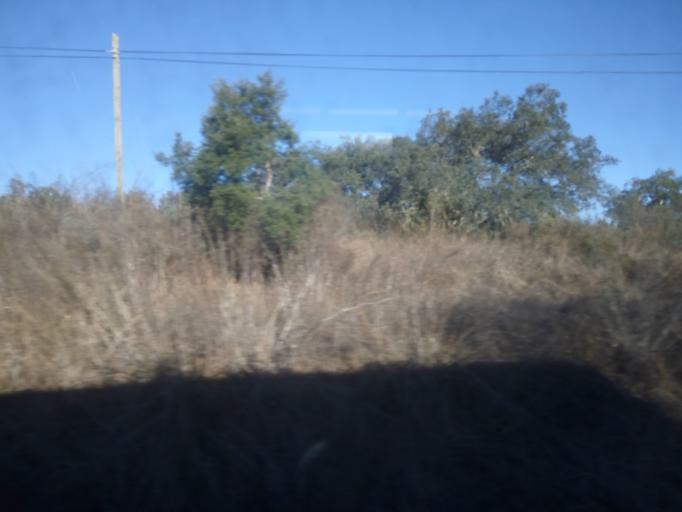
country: PT
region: Beja
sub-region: Odemira
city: Odemira
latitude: 37.5278
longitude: -8.4756
